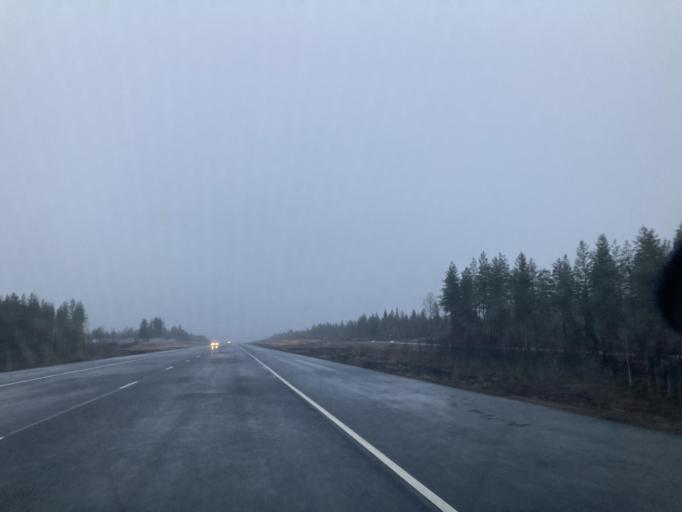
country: FI
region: Lapland
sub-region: Rovaniemi
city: Rovaniemi
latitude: 66.5824
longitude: 25.8004
